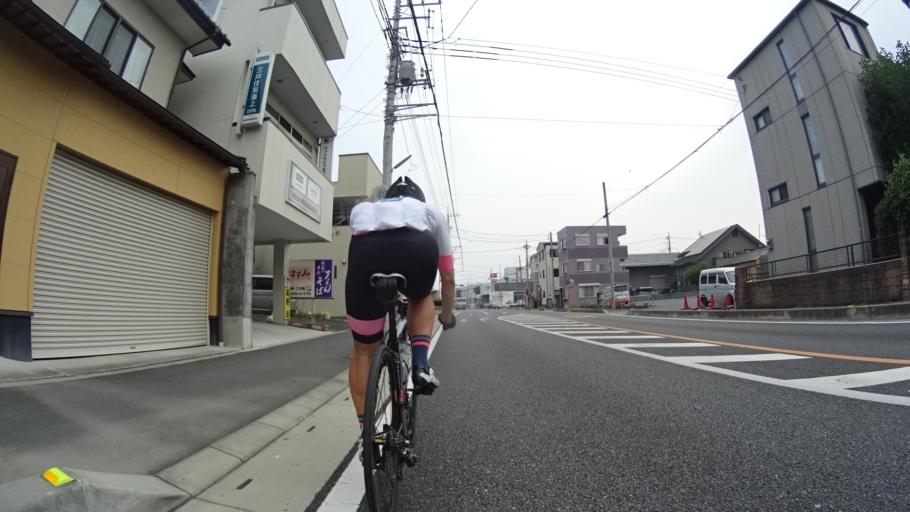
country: JP
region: Saitama
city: Chichibu
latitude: 36.0017
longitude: 139.0851
